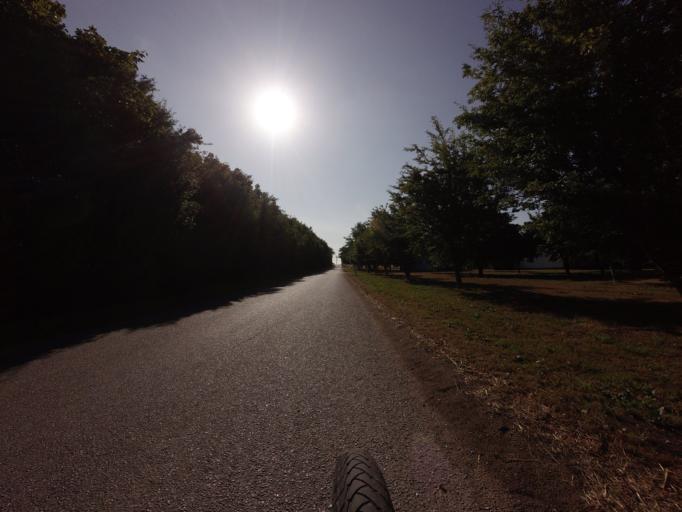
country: DK
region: North Denmark
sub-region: Hjorring Kommune
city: Vra
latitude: 57.3816
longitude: 9.9987
